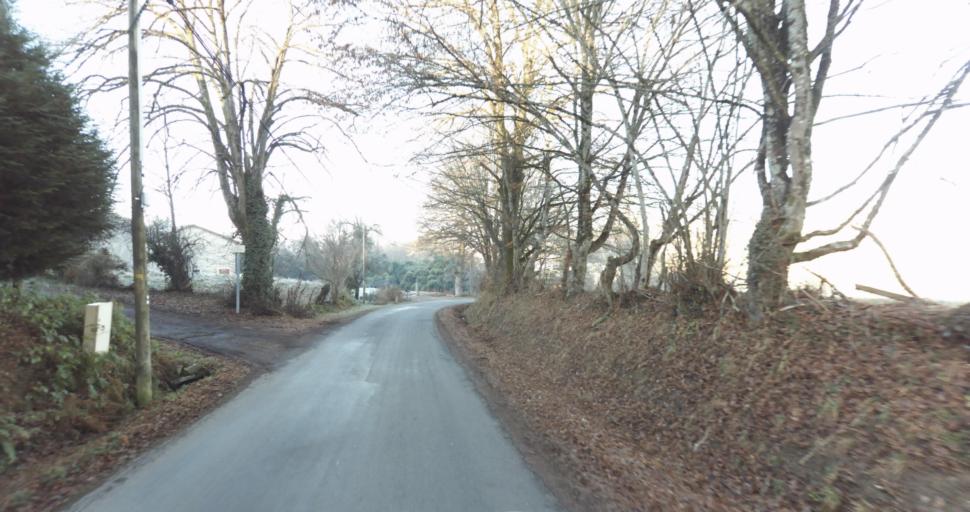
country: FR
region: Limousin
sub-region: Departement de la Haute-Vienne
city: Aixe-sur-Vienne
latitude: 45.8079
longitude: 1.1416
